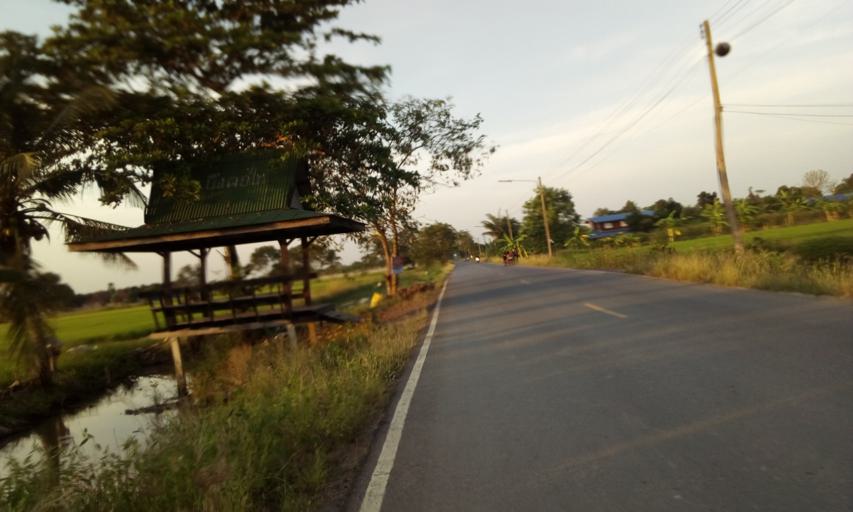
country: TH
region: Pathum Thani
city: Nong Suea
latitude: 14.0447
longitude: 100.8668
